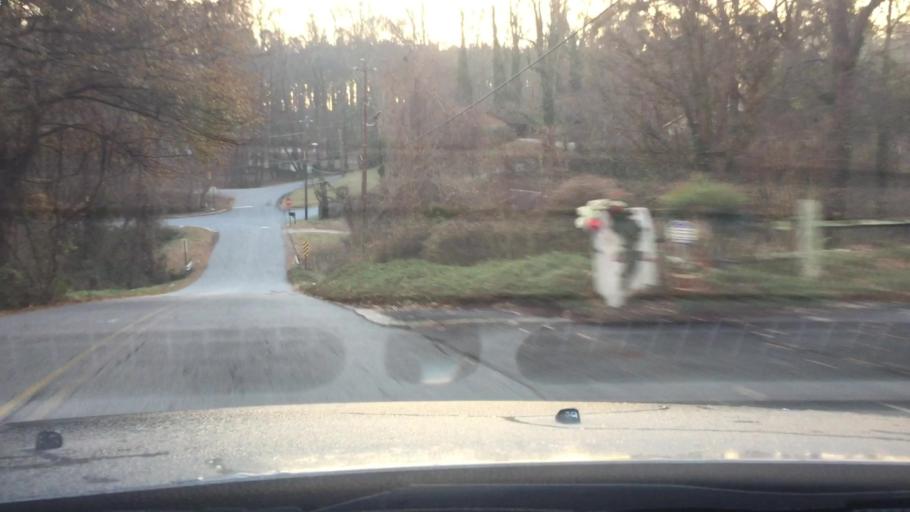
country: US
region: Georgia
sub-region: Cobb County
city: Marietta
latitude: 33.9866
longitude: -84.5502
